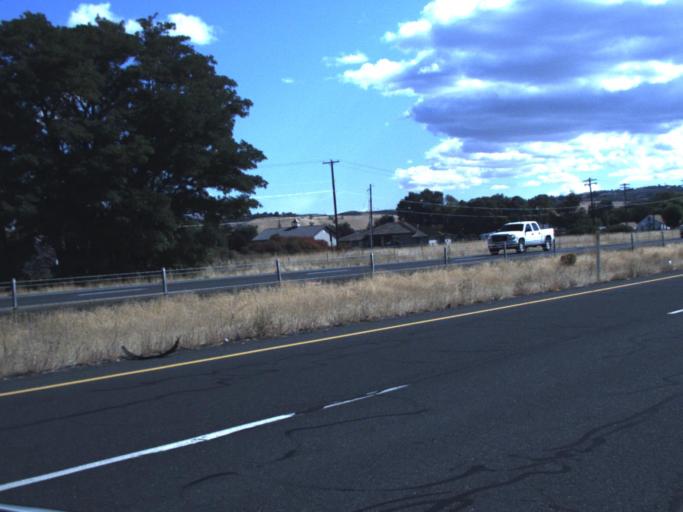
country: US
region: Washington
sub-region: Yakima County
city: Gleed
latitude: 46.6521
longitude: -120.6106
